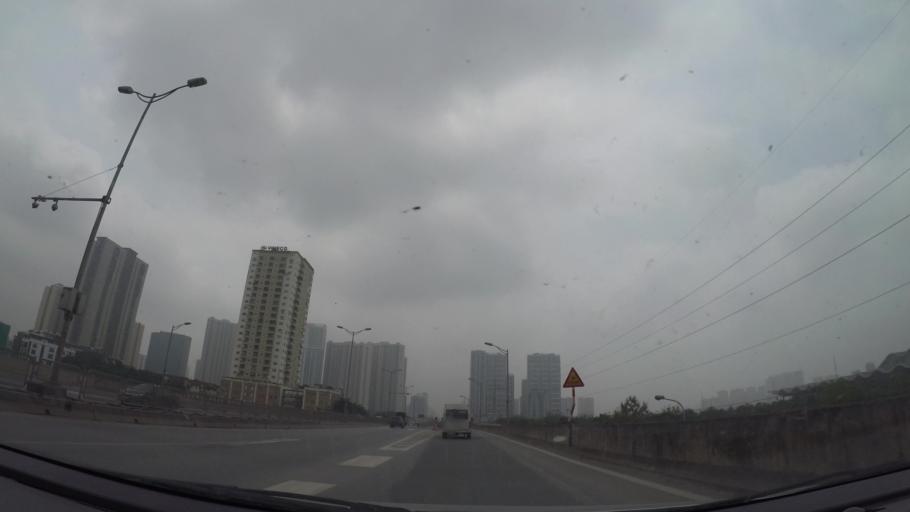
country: VN
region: Ha Noi
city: Thanh Xuan
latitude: 21.0096
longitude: 105.7886
